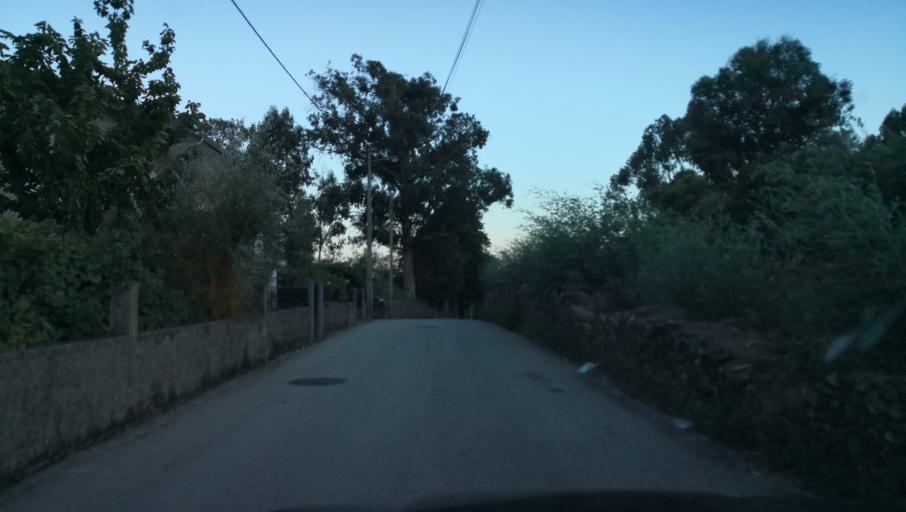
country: PT
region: Vila Real
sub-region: Vila Real
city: Vila Real
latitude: 41.3142
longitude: -7.7692
